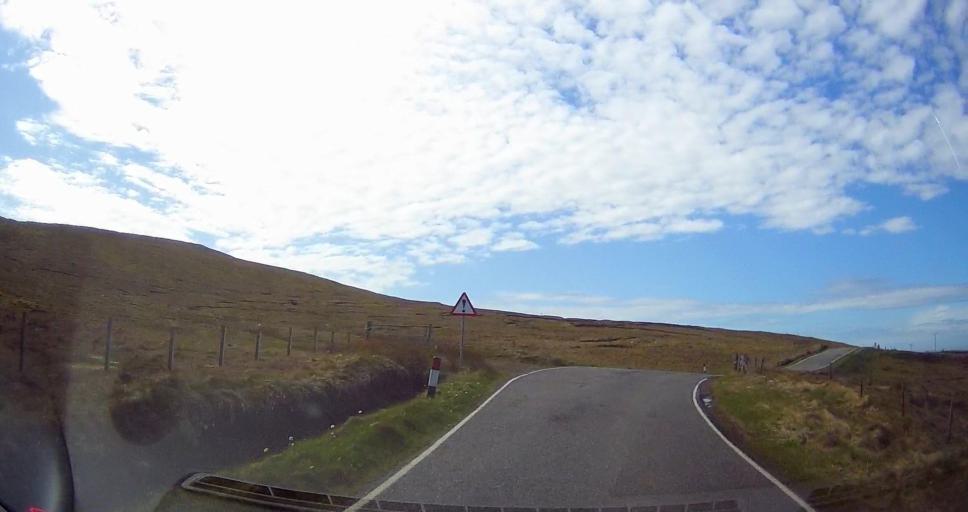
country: GB
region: Scotland
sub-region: Shetland Islands
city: Sandwick
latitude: 59.9813
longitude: -1.2920
